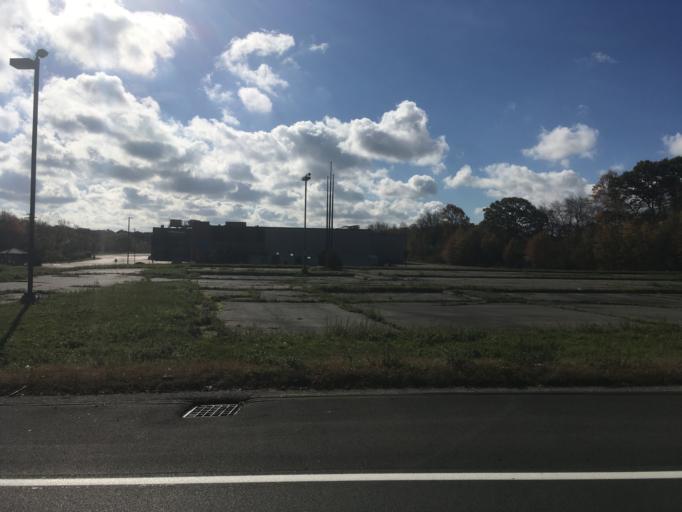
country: US
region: Rhode Island
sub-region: Providence County
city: Johnston
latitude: 41.7930
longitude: -71.5395
